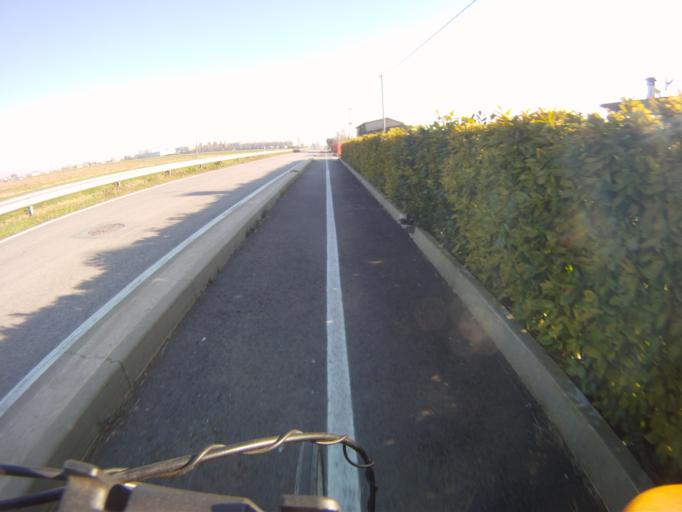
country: IT
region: Veneto
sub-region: Provincia di Padova
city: Brugine
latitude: 45.3099
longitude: 11.9859
